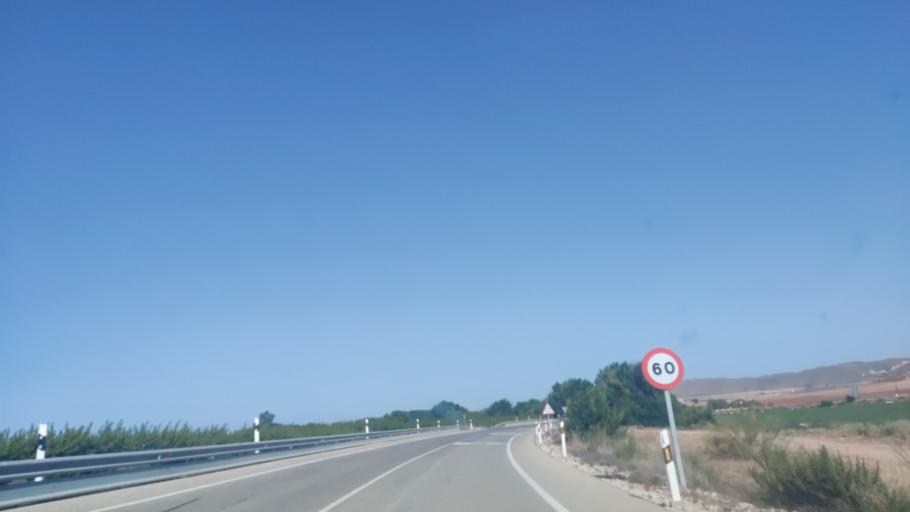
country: ES
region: Castille-La Mancha
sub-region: Provincia de Albacete
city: Hellin
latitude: 38.4925
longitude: -1.6390
